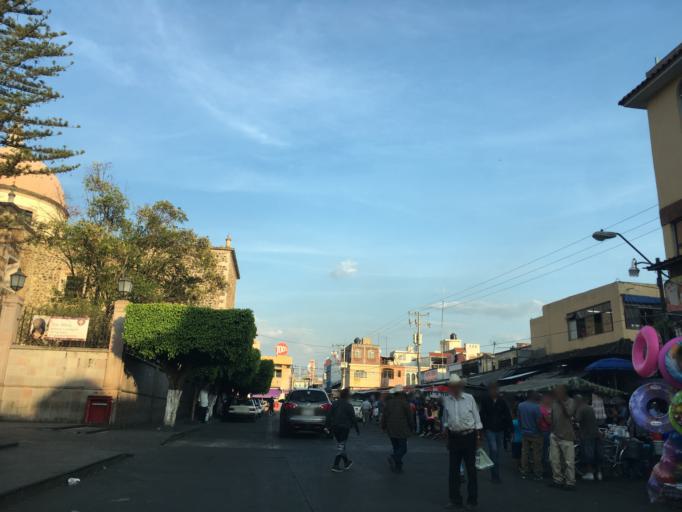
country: MX
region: Michoacan
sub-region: Los Reyes
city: La Higuerita (Colonia San Rafael)
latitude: 19.5889
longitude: -102.4740
